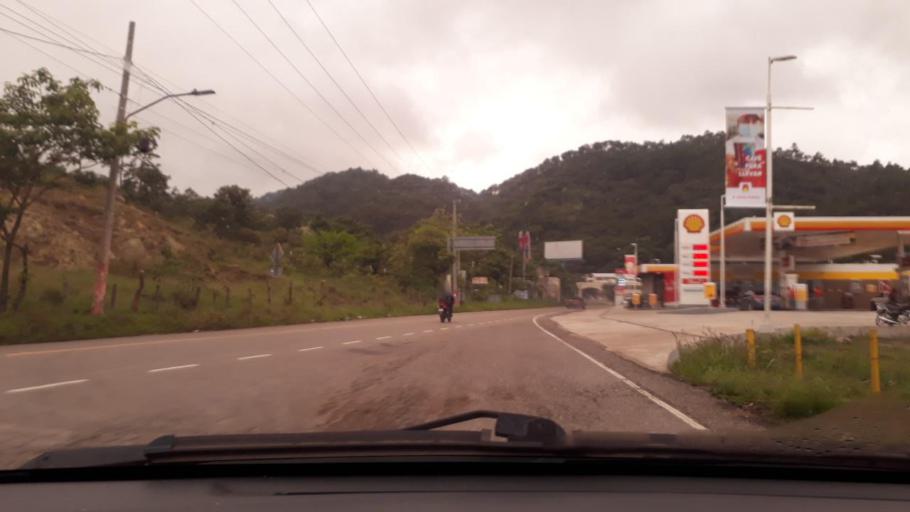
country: GT
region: Chiquimula
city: Esquipulas
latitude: 14.5614
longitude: -89.3565
